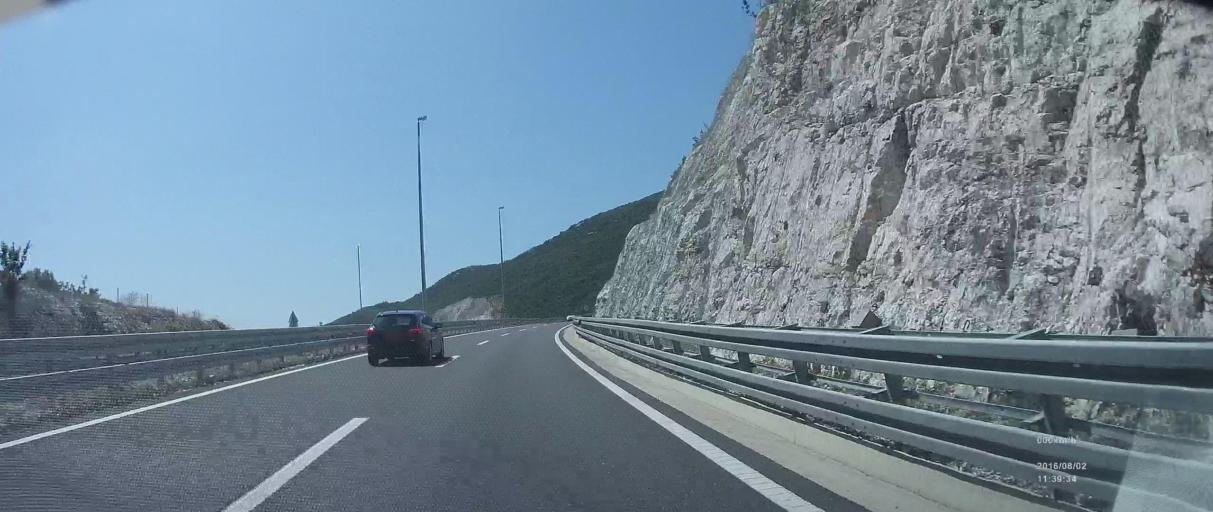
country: HR
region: Dubrovacko-Neretvanska
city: Komin
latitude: 43.0846
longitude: 17.4910
